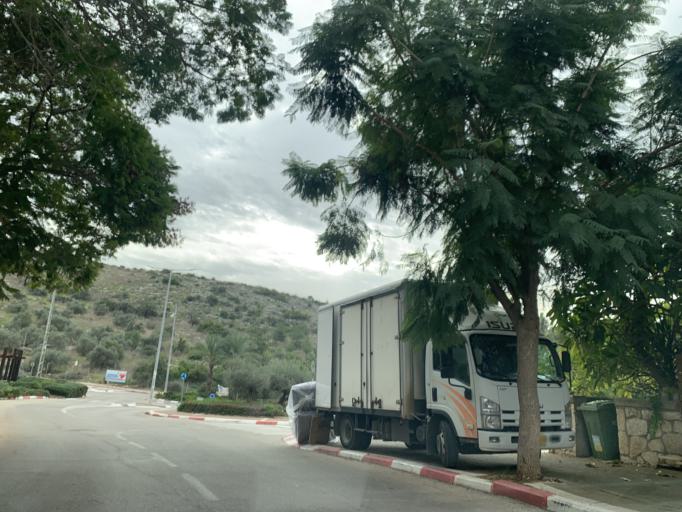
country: IL
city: Nirit
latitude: 32.1470
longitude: 34.9802
